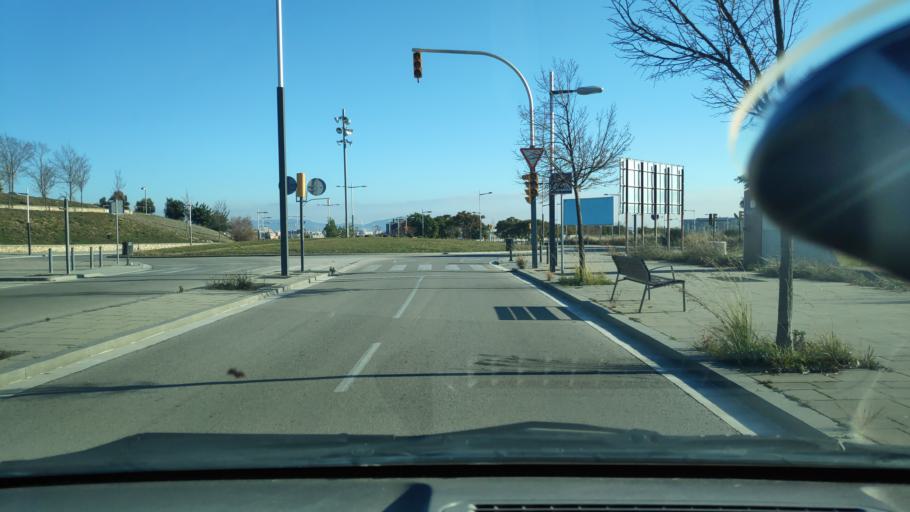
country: ES
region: Catalonia
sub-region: Provincia de Barcelona
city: Sant Quirze del Valles
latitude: 41.5418
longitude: 2.0841
